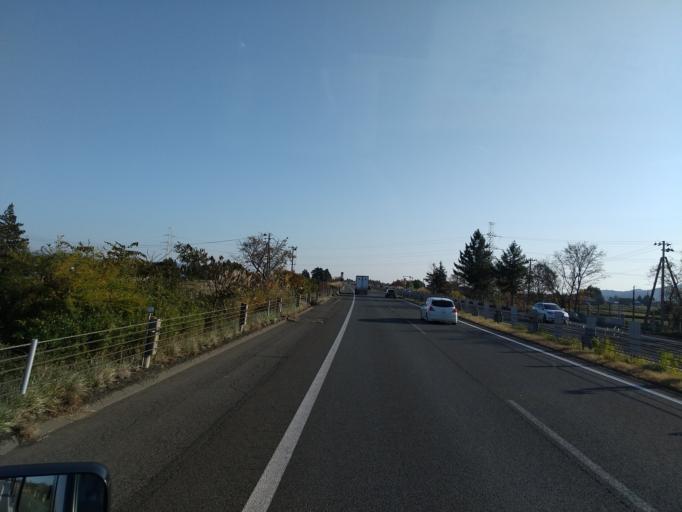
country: JP
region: Iwate
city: Morioka-shi
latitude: 39.5848
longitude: 141.1184
